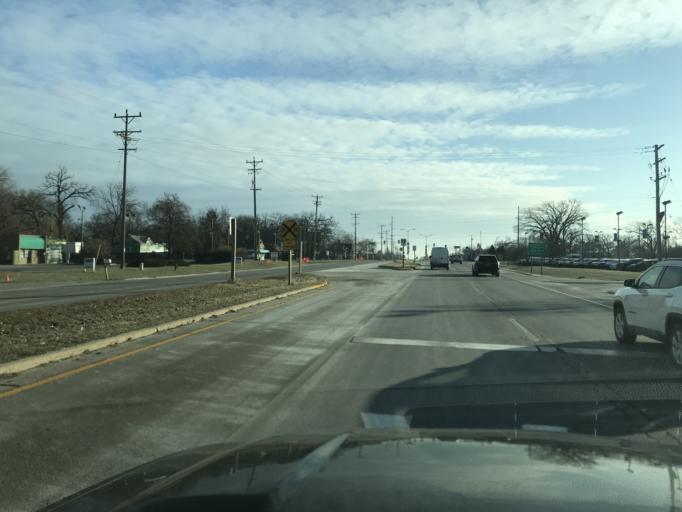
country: US
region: Wisconsin
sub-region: Kenosha County
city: Kenosha
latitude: 42.5663
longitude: -87.8725
